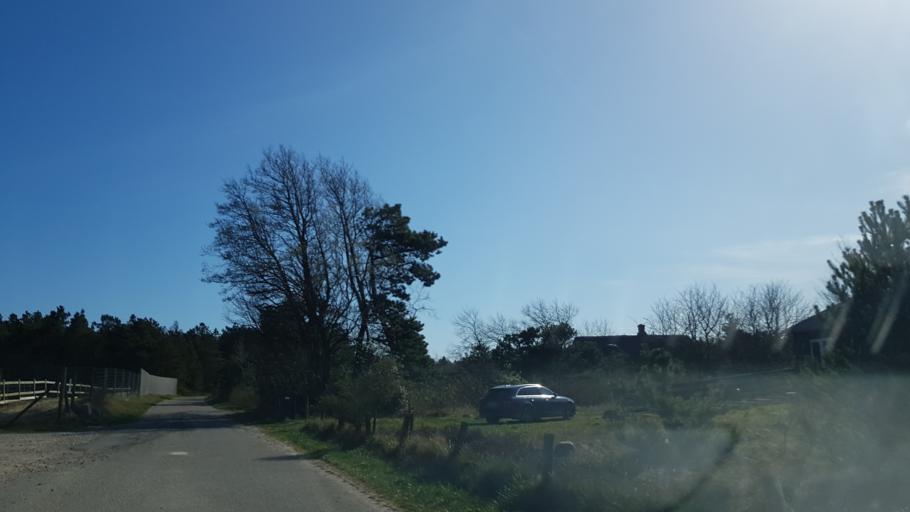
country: DE
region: Schleswig-Holstein
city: List
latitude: 55.0980
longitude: 8.5488
